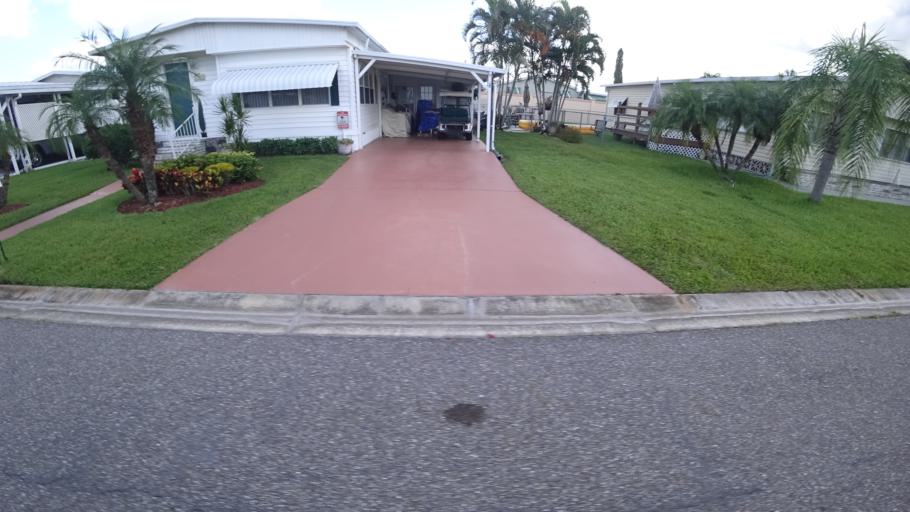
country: US
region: Florida
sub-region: Manatee County
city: West Samoset
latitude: 27.4529
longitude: -82.5614
